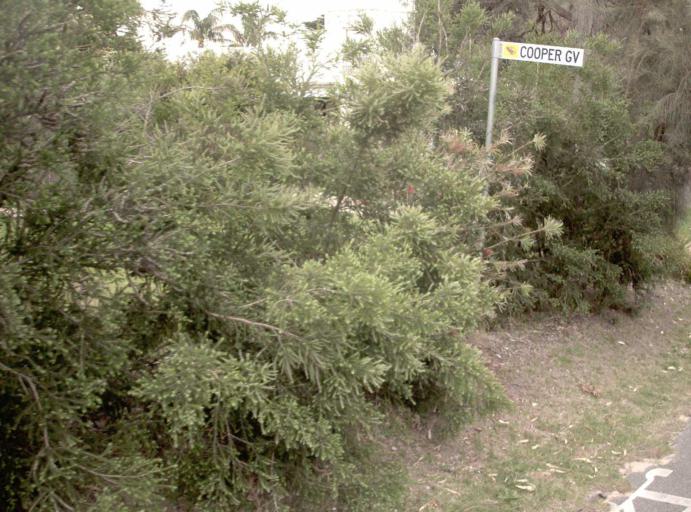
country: AU
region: Victoria
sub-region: Mornington Peninsula
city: Sorrento
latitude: -38.3372
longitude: 144.7410
